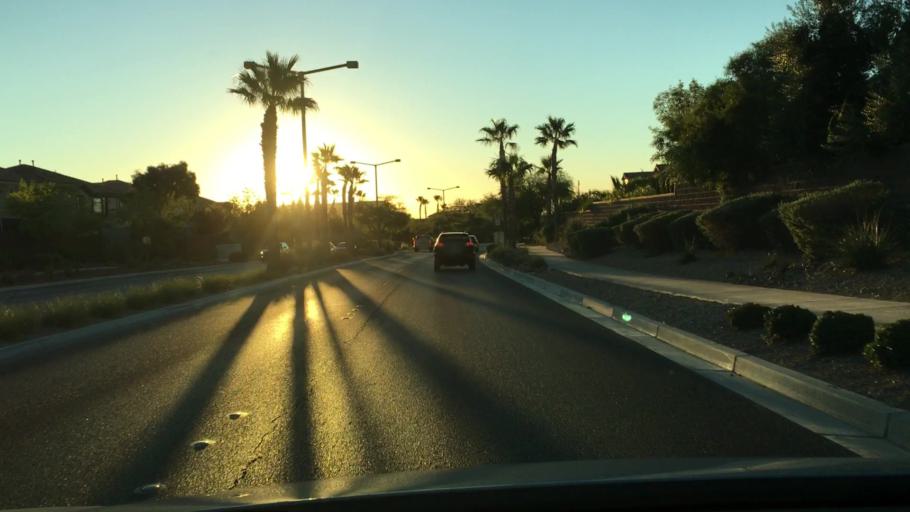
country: US
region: Nevada
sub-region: Clark County
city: Summerlin South
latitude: 36.1555
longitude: -115.3486
